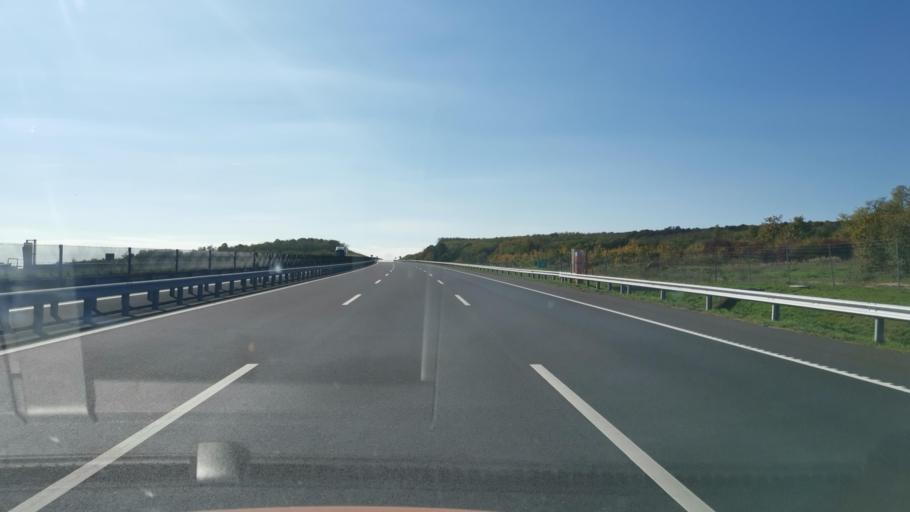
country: HU
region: Borsod-Abauj-Zemplen
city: Aszalo
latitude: 48.2253
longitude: 20.9418
